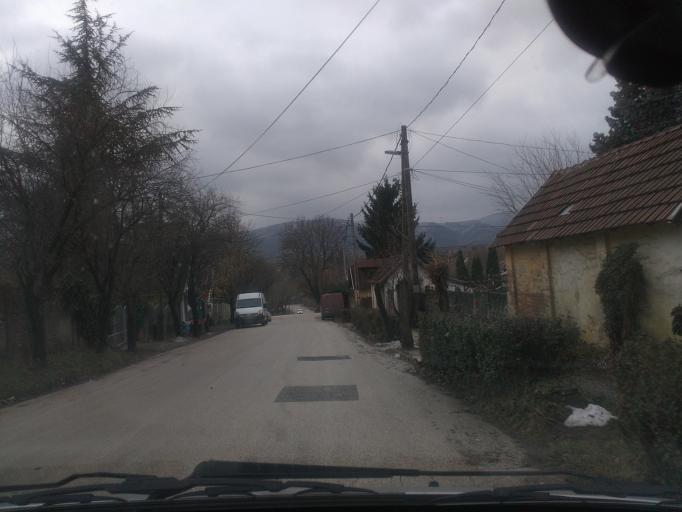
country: HU
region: Pest
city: Pilisvorosvar
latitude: 47.6138
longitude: 18.9195
